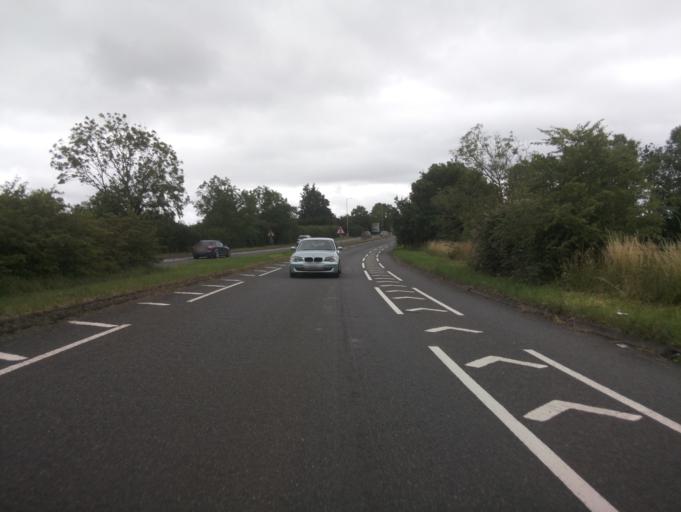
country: GB
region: England
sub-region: Gloucestershire
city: Tewkesbury
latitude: 51.9603
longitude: -2.1567
